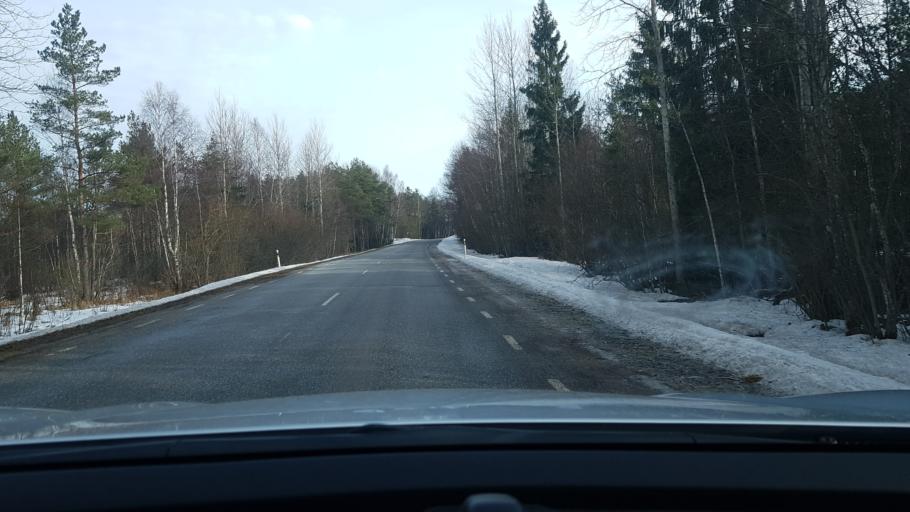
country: EE
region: Saare
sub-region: Kuressaare linn
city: Kuressaare
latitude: 58.4234
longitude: 22.6697
